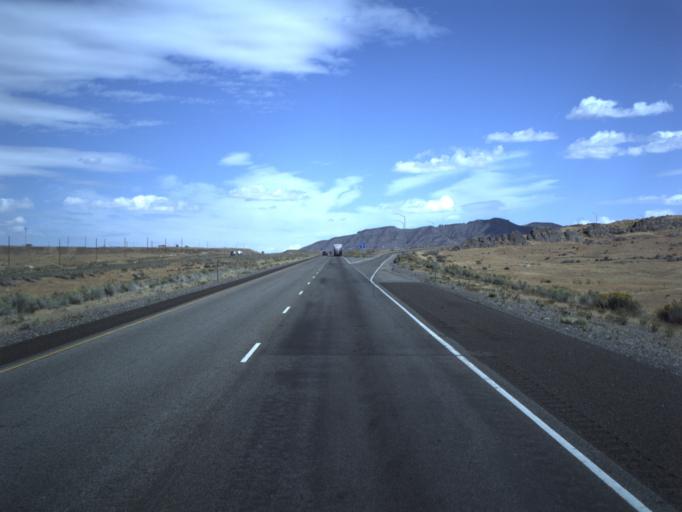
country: US
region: Utah
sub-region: Tooele County
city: Grantsville
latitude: 40.7556
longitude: -113.0259
